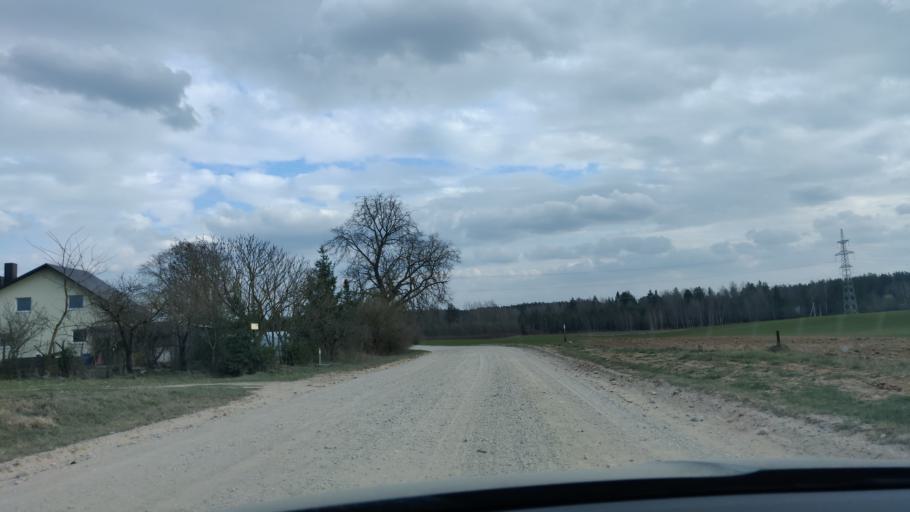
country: LT
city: Lentvaris
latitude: 54.6104
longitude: 25.0710
